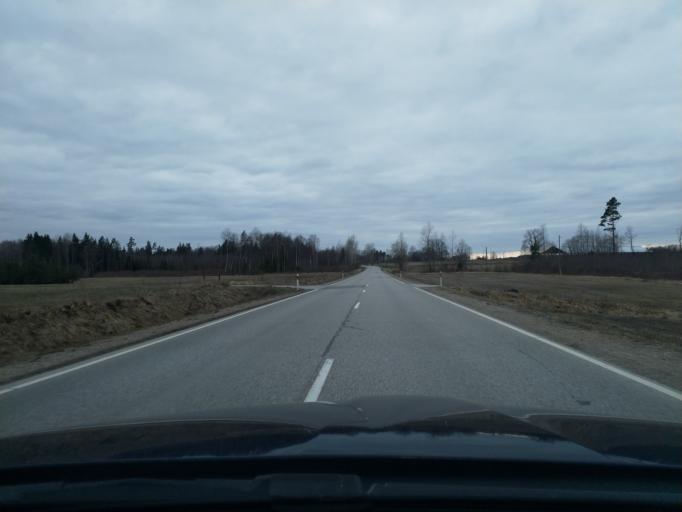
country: LV
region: Kuldigas Rajons
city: Kuldiga
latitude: 56.9706
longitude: 22.0380
